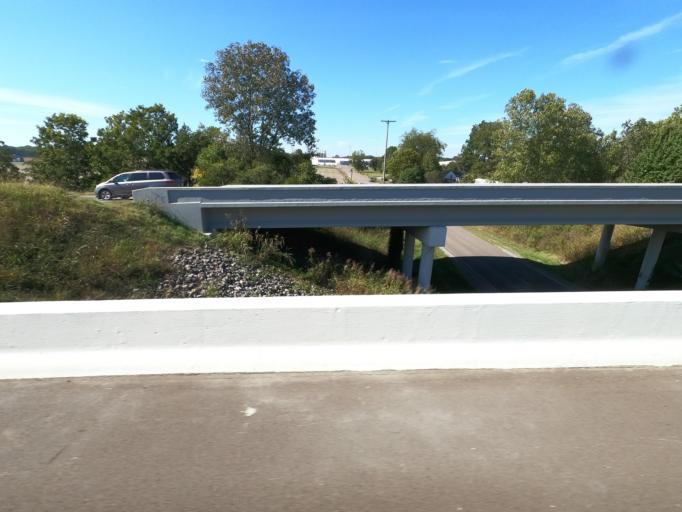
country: US
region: Tennessee
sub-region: Dyer County
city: Dyersburg
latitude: 36.0488
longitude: -89.3349
